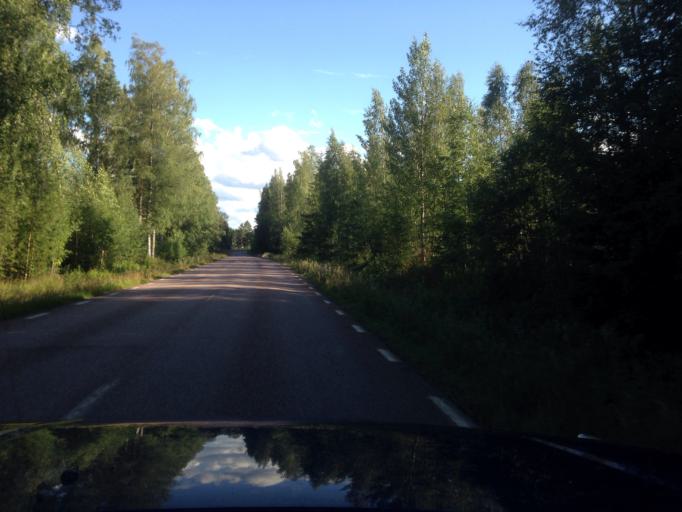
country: SE
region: Dalarna
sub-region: Ludvika Kommun
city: Grangesberg
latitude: 60.1914
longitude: 14.9686
